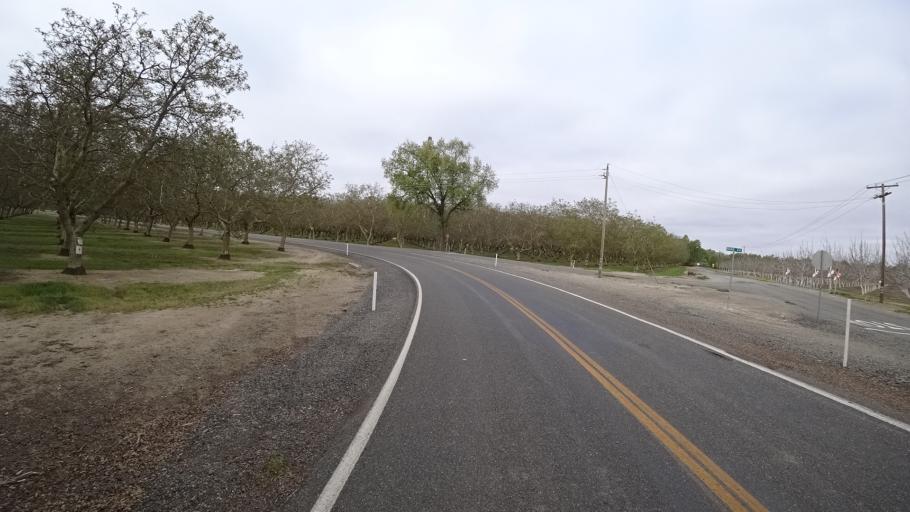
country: US
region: California
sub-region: Colusa County
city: Colusa
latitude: 39.4020
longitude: -121.9975
